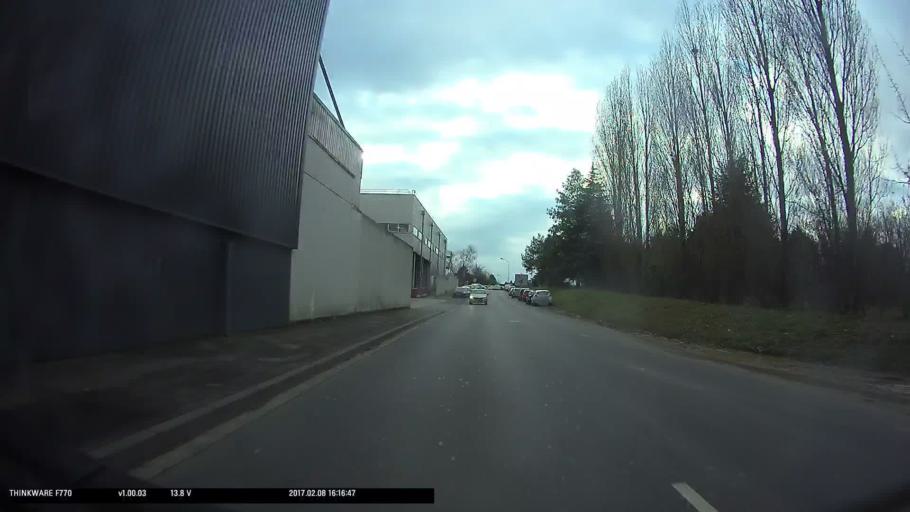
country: FR
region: Ile-de-France
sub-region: Departement du Val-d'Oise
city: Osny
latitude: 49.0783
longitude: 2.0787
